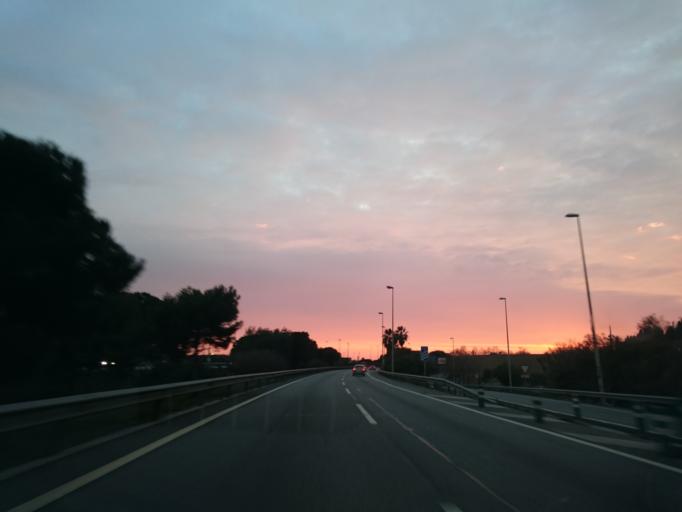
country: ES
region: Catalonia
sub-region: Provincia de Barcelona
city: Sants-Montjuic
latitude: 41.3540
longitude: 2.1586
